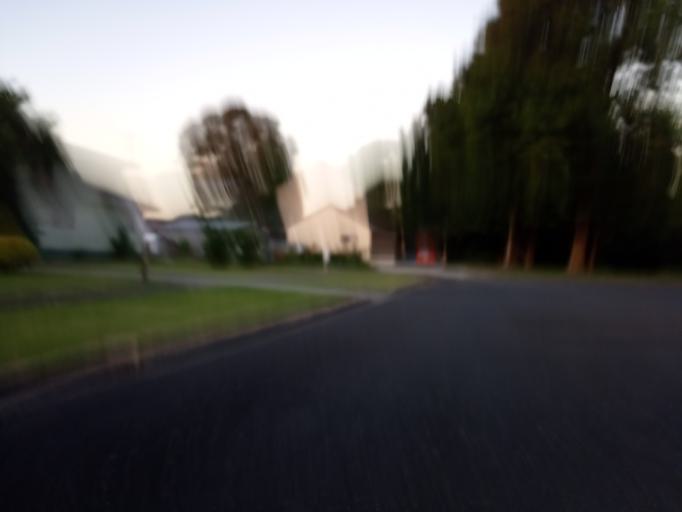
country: NZ
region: Gisborne
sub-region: Gisborne District
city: Gisborne
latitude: -38.6457
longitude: 177.9919
